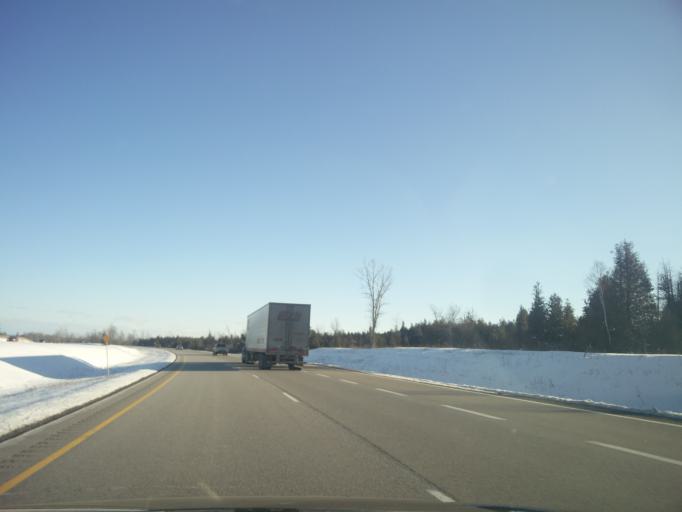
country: CA
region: Ontario
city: Prescott
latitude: 44.9811
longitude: -75.6100
